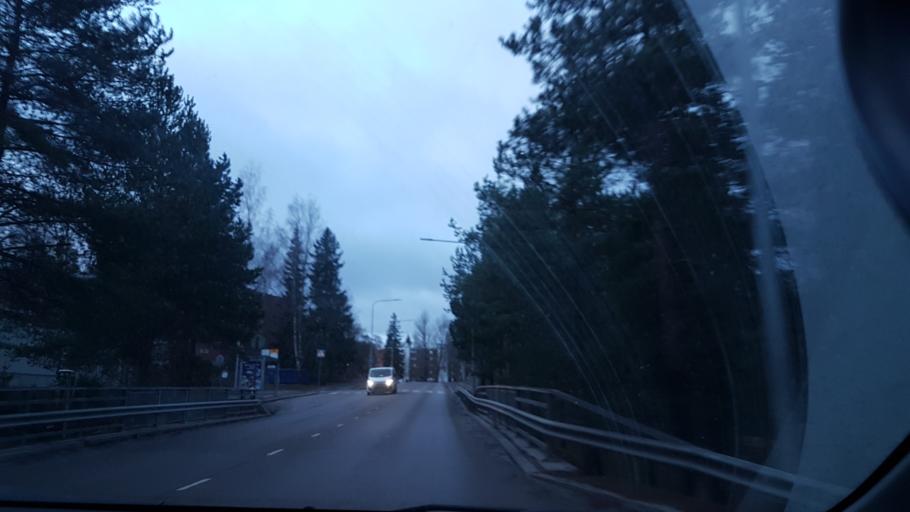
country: FI
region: Uusimaa
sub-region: Helsinki
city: Vantaa
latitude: 60.2818
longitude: 25.1125
